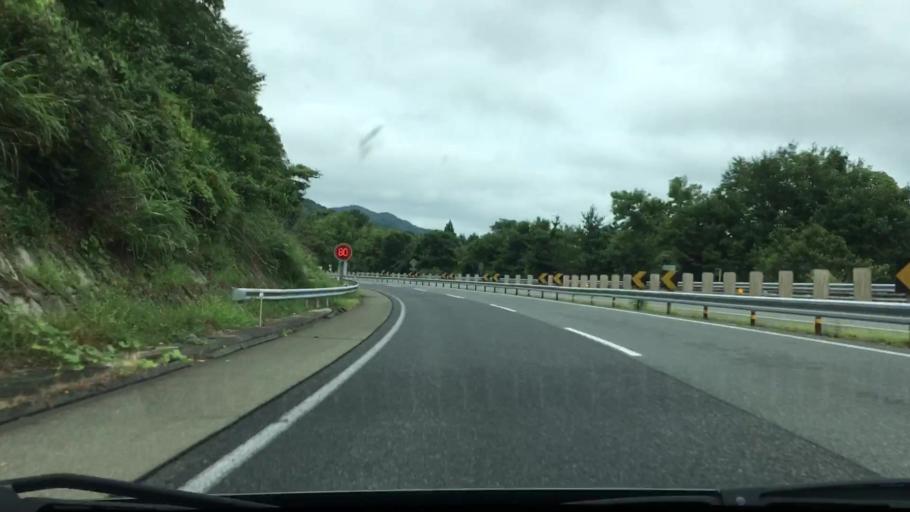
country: JP
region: Hiroshima
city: Shobara
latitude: 34.8414
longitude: 133.0838
